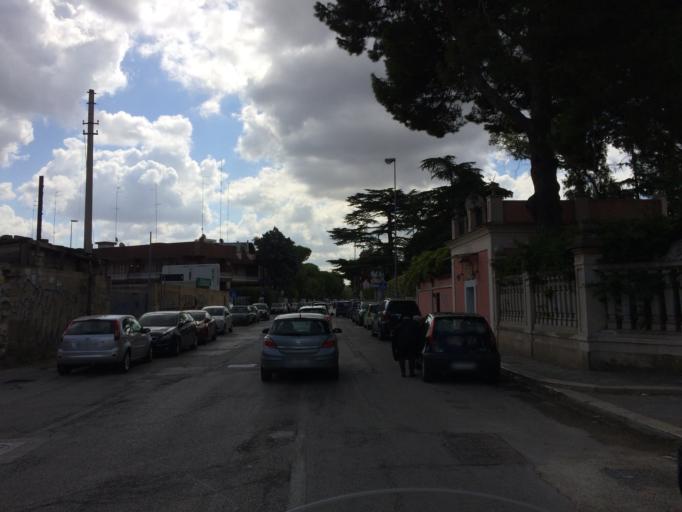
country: IT
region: Apulia
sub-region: Provincia di Bari
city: Bari
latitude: 41.0994
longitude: 16.8805
